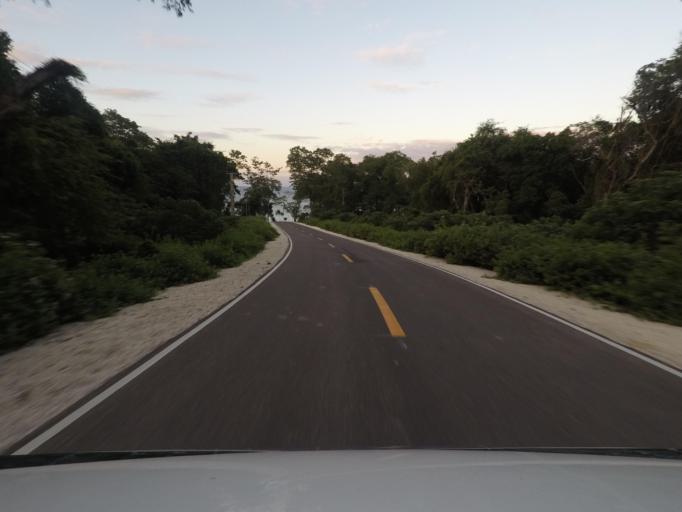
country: TL
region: Lautem
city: Lospalos
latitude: -8.4131
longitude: 127.2988
